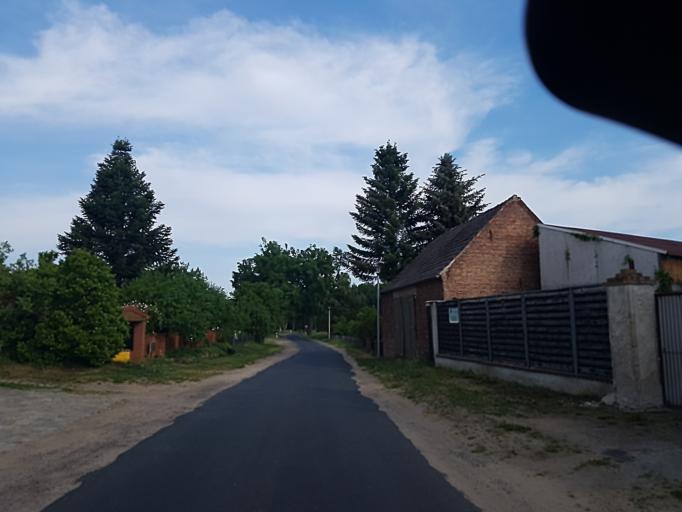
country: DE
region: Brandenburg
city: Belzig
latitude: 52.0439
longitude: 12.5741
